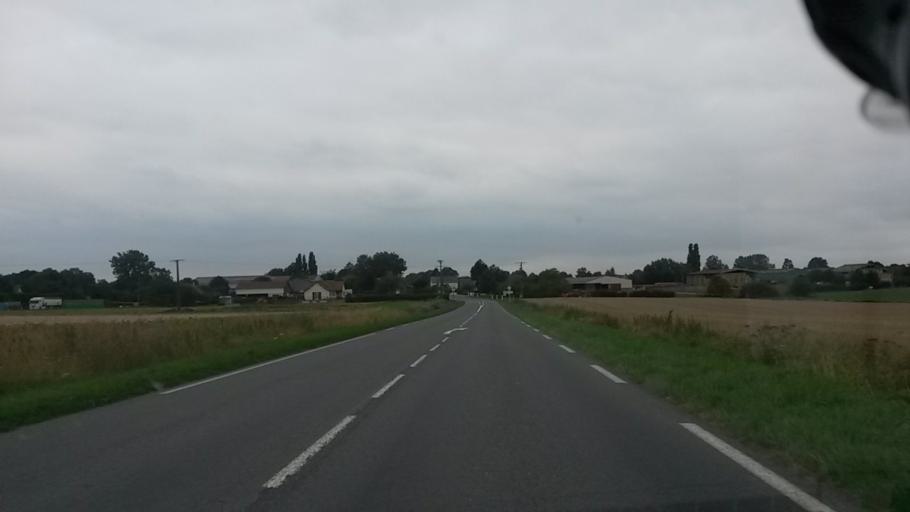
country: FR
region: Picardie
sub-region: Departement de la Somme
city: Hornoy-le-Bourg
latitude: 49.7807
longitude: 1.8981
